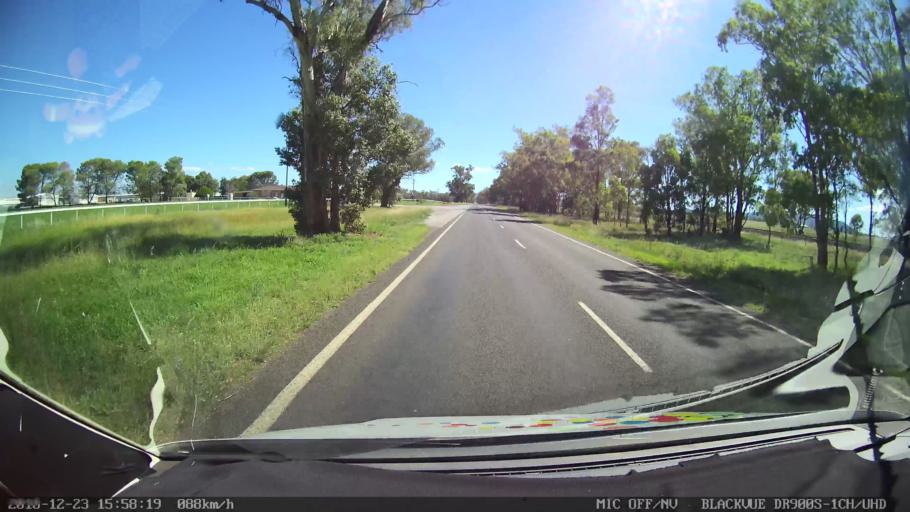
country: AU
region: New South Wales
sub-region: Tamworth Municipality
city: Phillip
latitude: -31.1869
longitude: 150.8427
